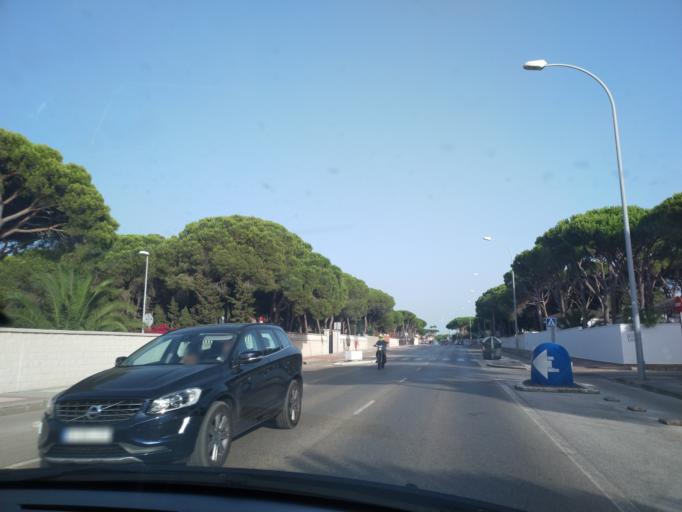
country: ES
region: Andalusia
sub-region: Provincia de Cadiz
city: Chiclana de la Frontera
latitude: 36.3788
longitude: -6.1897
